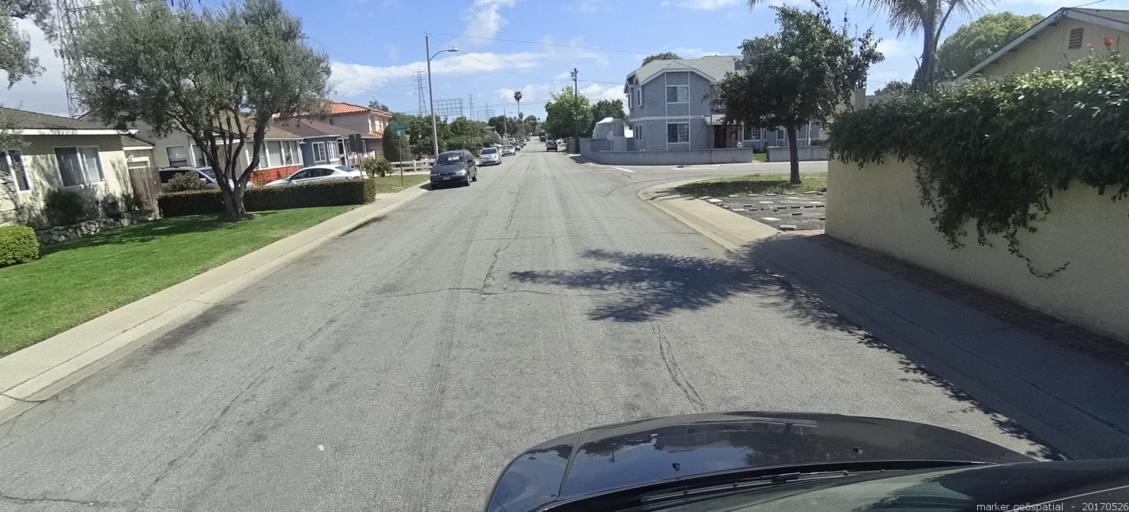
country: US
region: California
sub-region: Los Angeles County
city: Lawndale
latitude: 33.8857
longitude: -118.3665
